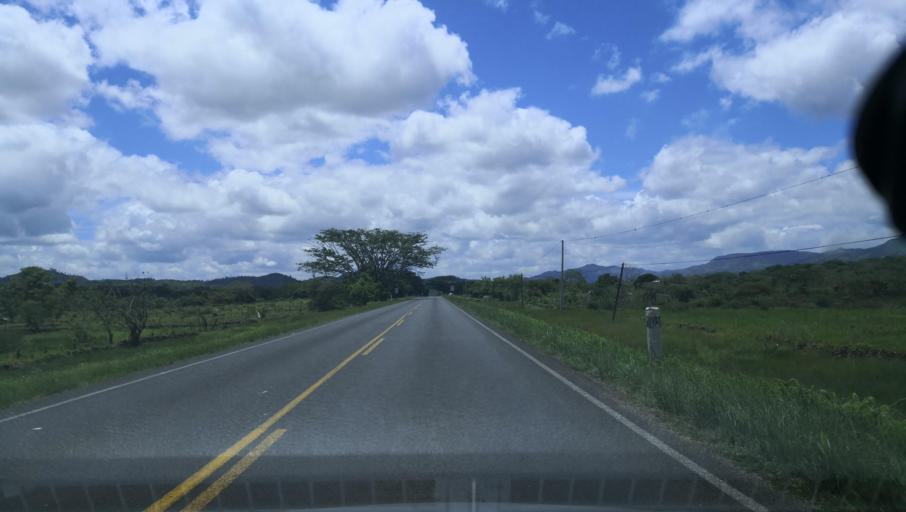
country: NI
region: Esteli
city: Esteli
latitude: 13.2225
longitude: -86.3794
